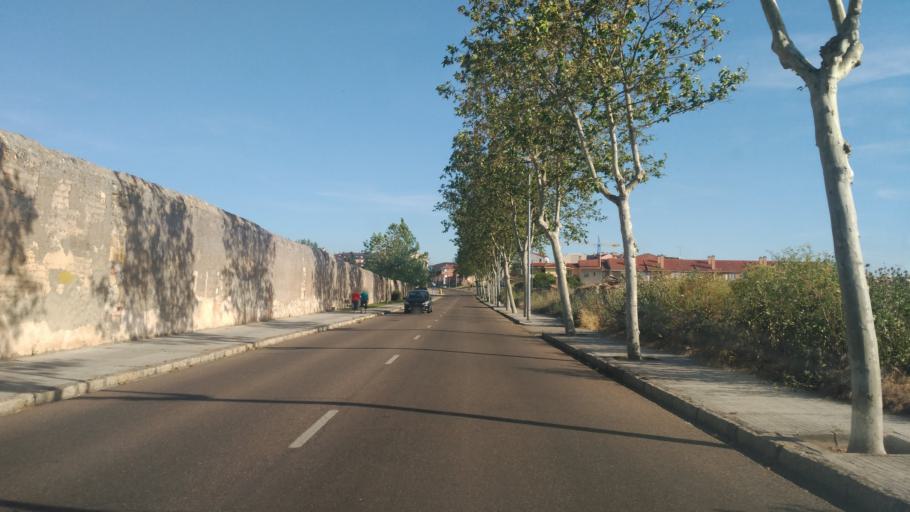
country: ES
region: Castille and Leon
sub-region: Provincia de Zamora
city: Zamora
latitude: 41.4957
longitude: -5.7469
